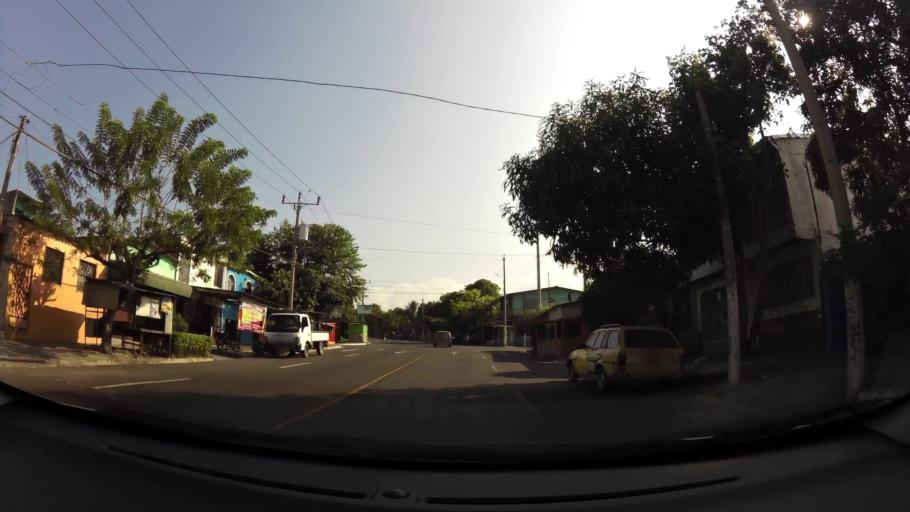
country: SV
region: San Salvador
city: Ilopango
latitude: 13.7147
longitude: -89.1073
